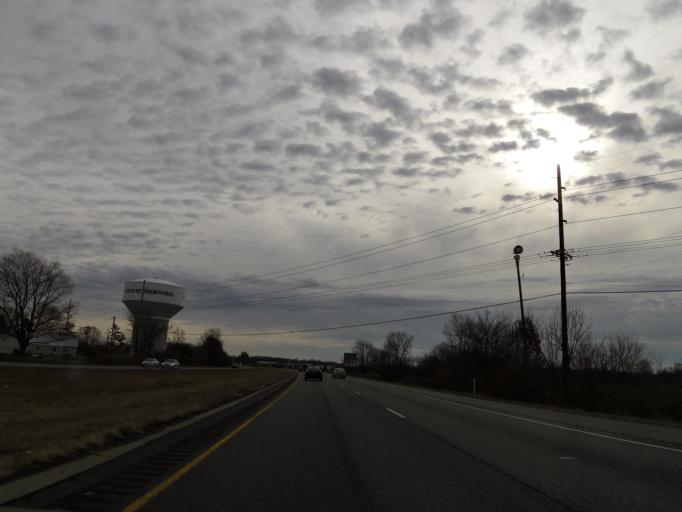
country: US
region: Indiana
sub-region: Hendricks County
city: Brownsburg
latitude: 39.8658
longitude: -86.4150
